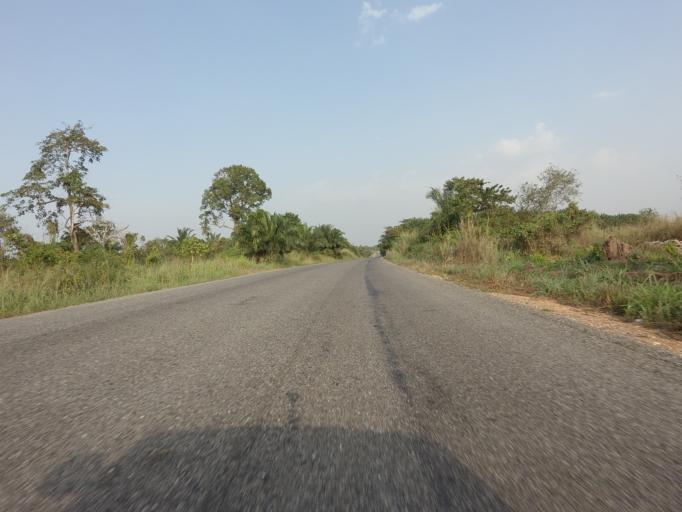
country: GH
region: Volta
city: Ho
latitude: 6.4393
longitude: 0.1986
